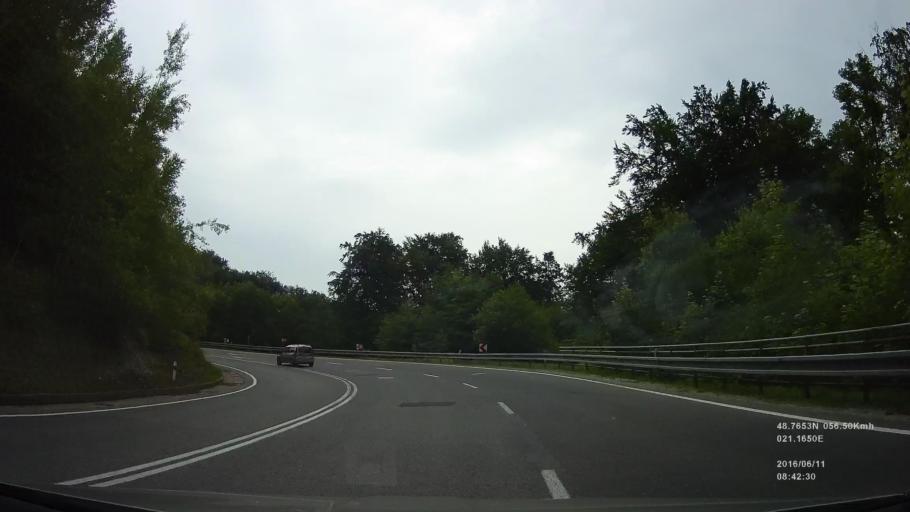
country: SK
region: Kosicky
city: Kosice
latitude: 48.7507
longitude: 21.2261
